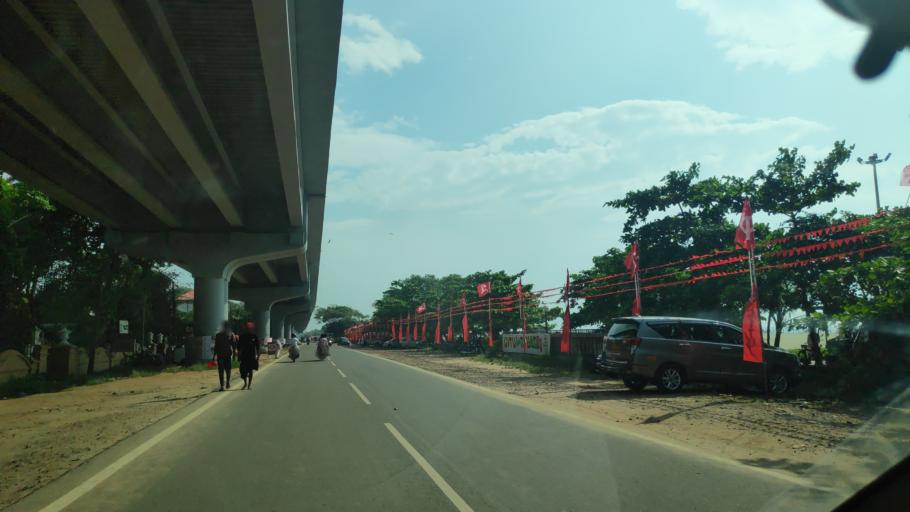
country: IN
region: Kerala
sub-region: Alappuzha
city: Alleppey
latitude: 9.4944
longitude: 76.3183
